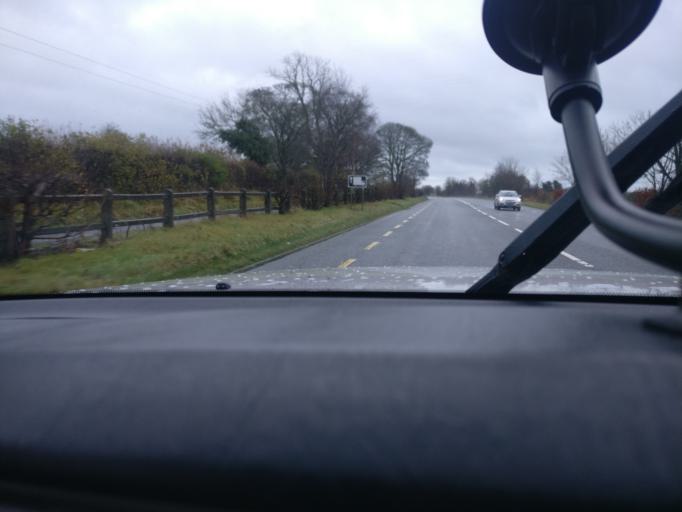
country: IE
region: Leinster
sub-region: An Mhi
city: Longwood
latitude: 53.4271
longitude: -6.9082
